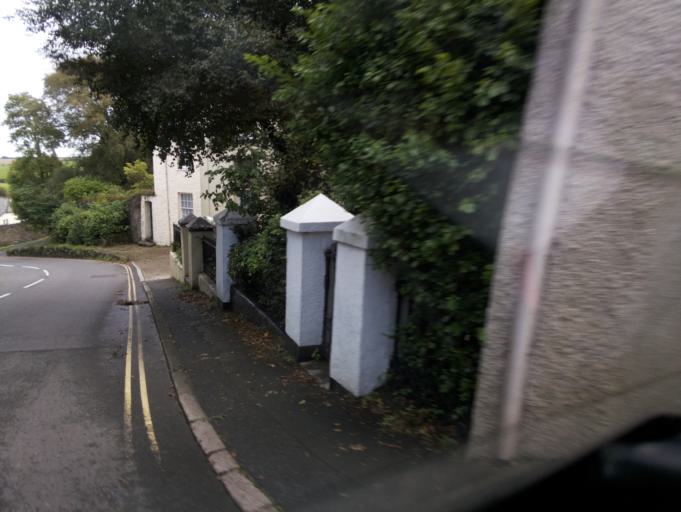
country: GB
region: England
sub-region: Devon
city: Modbury
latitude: 50.3497
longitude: -3.8900
